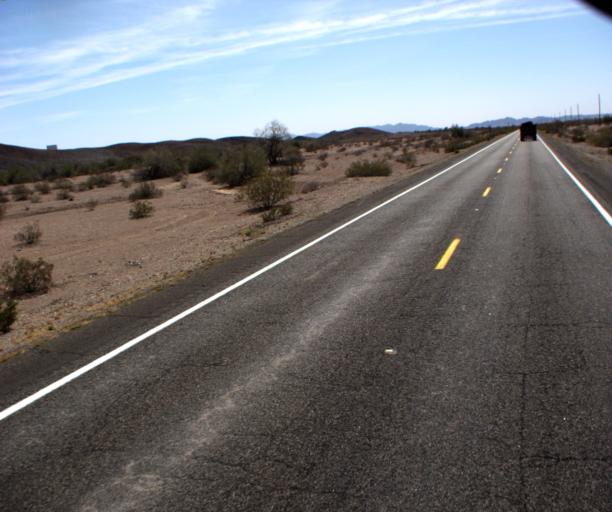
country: US
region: Arizona
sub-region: Yuma County
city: Fortuna Foothills
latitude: 32.9337
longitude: -114.3111
